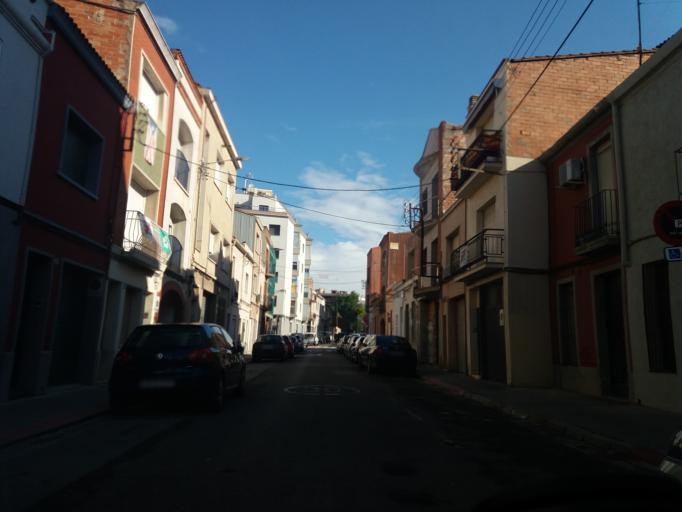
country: ES
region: Catalonia
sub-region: Provincia de Barcelona
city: Sabadell
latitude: 41.5575
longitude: 2.1009
